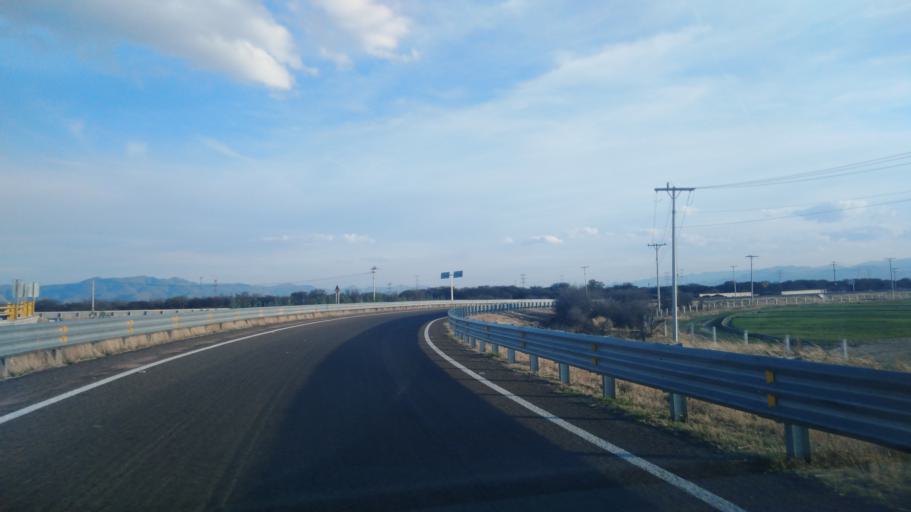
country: MX
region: Durango
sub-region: Durango
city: Jose Refugio Salcido
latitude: 24.0197
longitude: -104.5215
